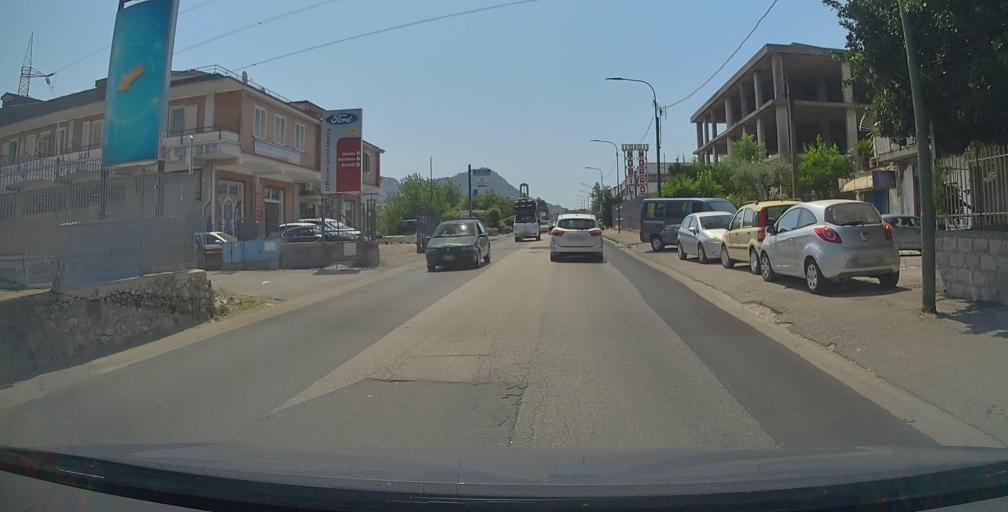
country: IT
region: Campania
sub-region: Provincia di Salerno
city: Nocera Superiore
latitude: 40.7265
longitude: 14.6919
